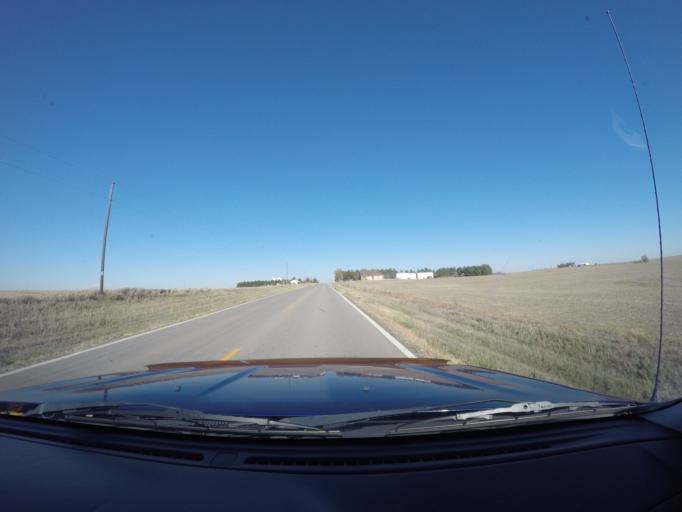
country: US
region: Kansas
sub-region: Nemaha County
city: Seneca
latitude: 39.8547
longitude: -96.2584
